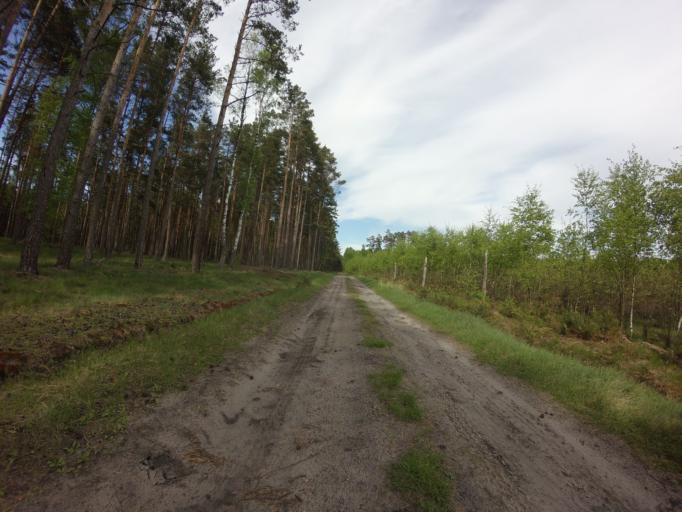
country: PL
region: West Pomeranian Voivodeship
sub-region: Powiat choszczenski
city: Drawno
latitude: 53.1880
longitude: 15.7283
